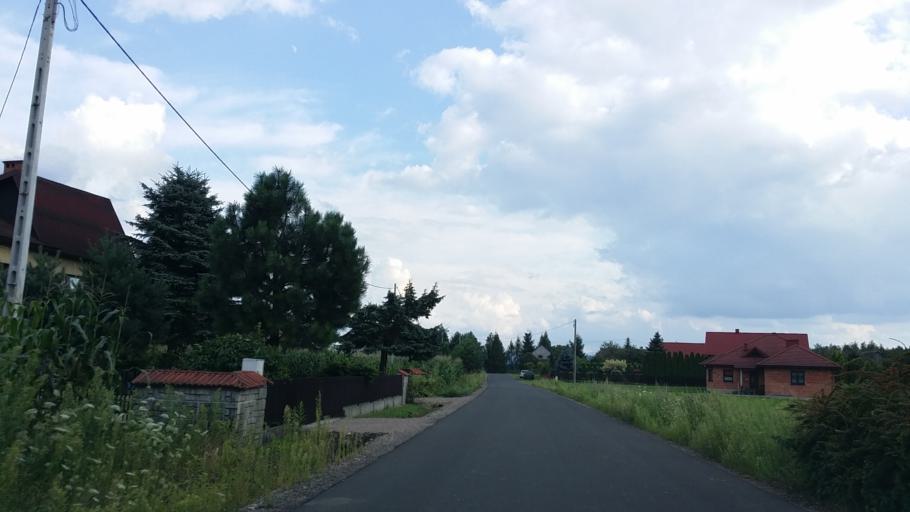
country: PL
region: Lesser Poland Voivodeship
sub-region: Powiat wadowicki
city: Bachowice
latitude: 49.9738
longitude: 19.4788
